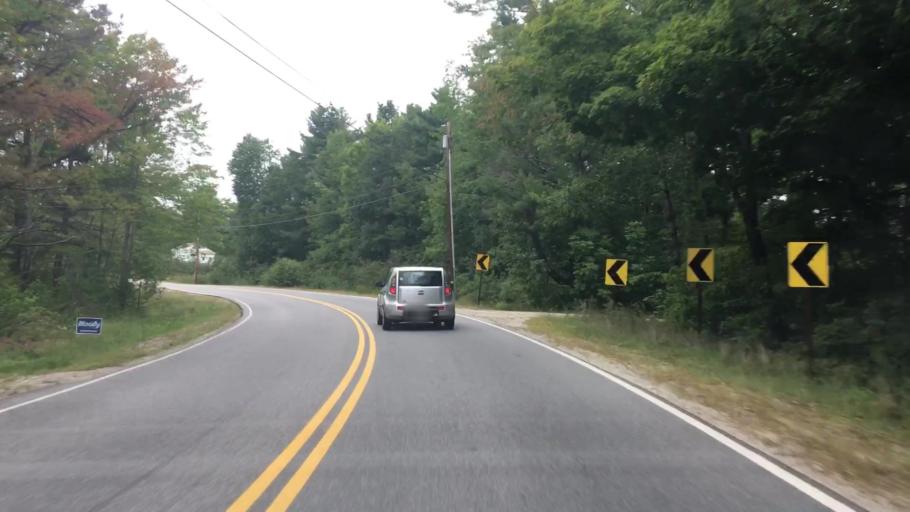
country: US
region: Maine
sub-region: Cumberland County
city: Cumberland Center
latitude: 43.8721
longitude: -70.2325
